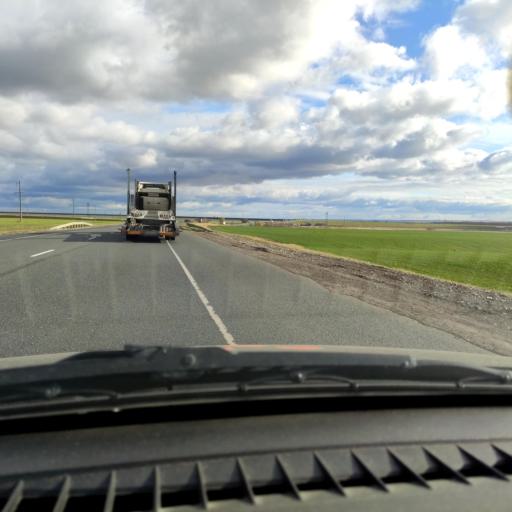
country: RU
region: Samara
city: Varlamovo
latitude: 53.2118
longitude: 48.4000
